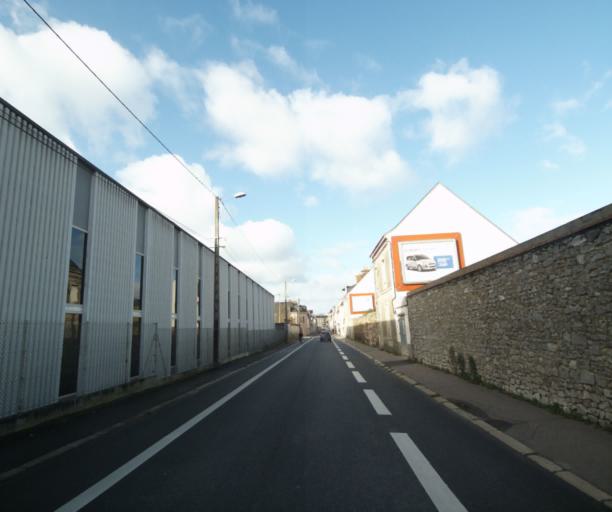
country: FR
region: Pays de la Loire
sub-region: Departement de la Sarthe
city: Le Mans
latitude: 47.9992
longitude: 0.1870
